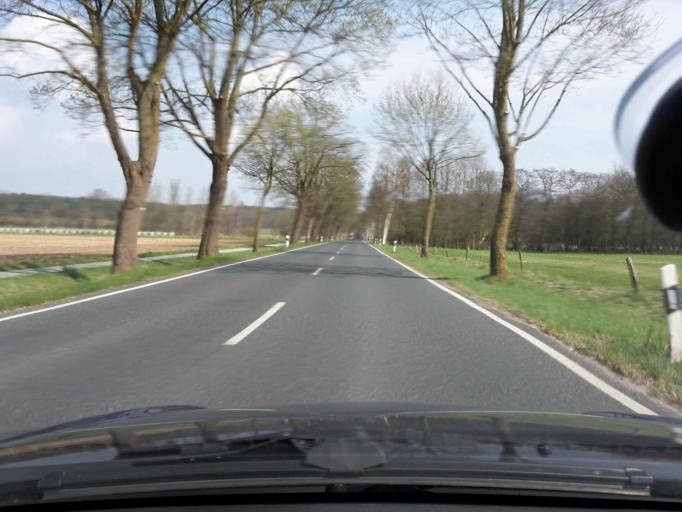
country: DE
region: Lower Saxony
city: Jesteburg
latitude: 53.2997
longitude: 9.9333
